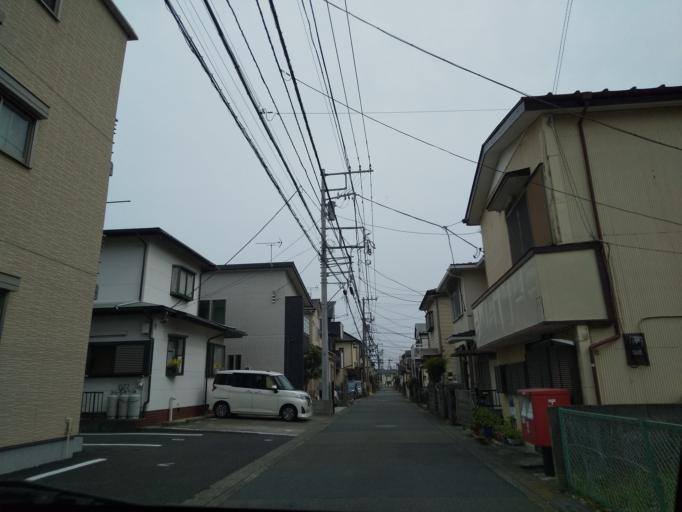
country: JP
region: Kanagawa
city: Minami-rinkan
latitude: 35.4649
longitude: 139.4263
